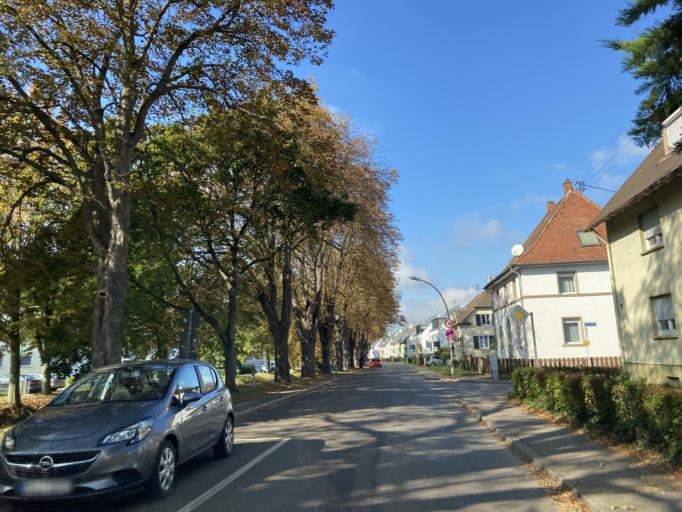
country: DE
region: Baden-Wuerttemberg
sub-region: Freiburg Region
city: Heitersheim
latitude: 47.8770
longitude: 7.6523
